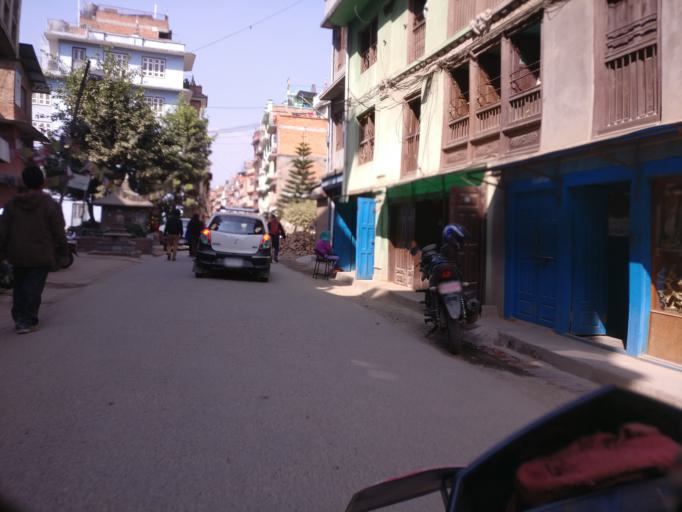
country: NP
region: Central Region
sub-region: Bagmati Zone
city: Patan
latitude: 27.6690
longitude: 85.3267
